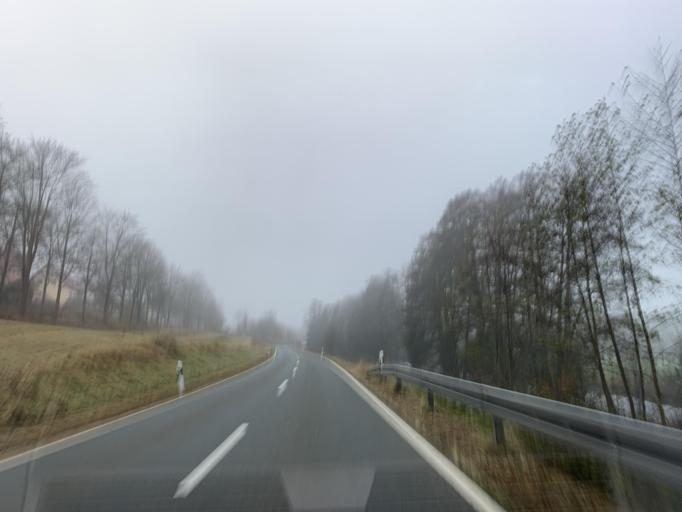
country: DE
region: Bavaria
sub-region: Upper Palatinate
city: Neunburg vorm Wald
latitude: 49.3560
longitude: 12.3937
